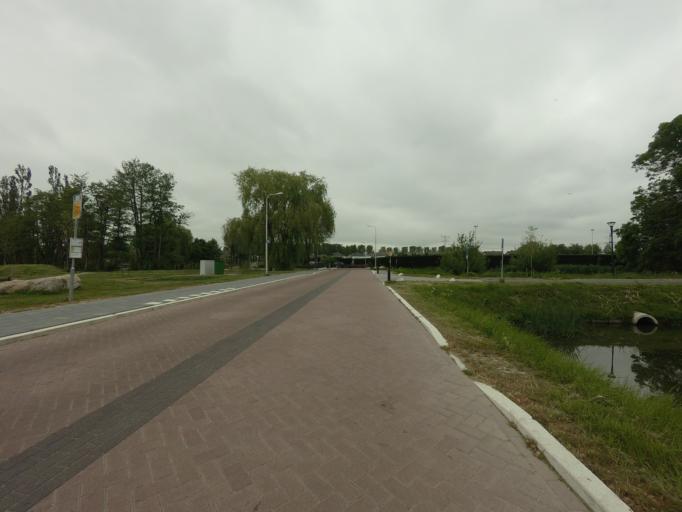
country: NL
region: South Holland
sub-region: Gemeente Spijkenisse
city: Spijkenisse
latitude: 51.8072
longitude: 4.3446
